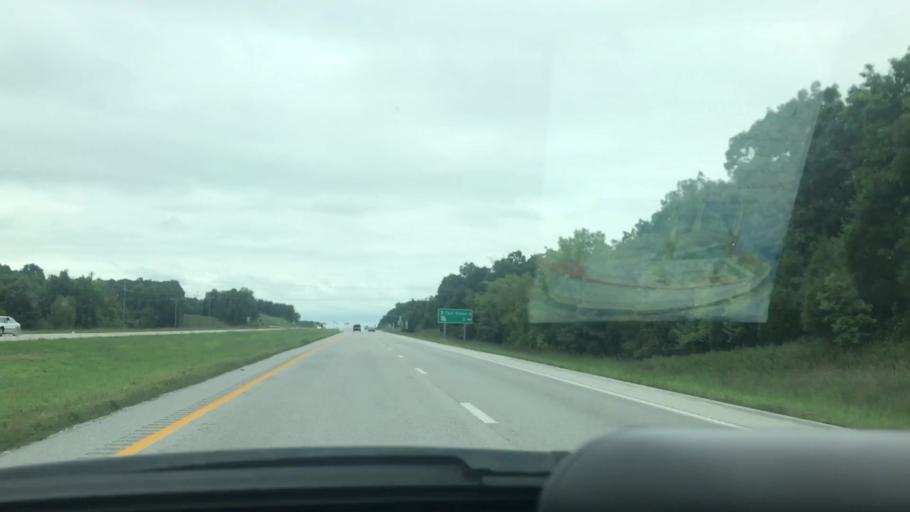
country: US
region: Missouri
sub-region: Greene County
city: Fair Grove
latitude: 37.3241
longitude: -93.1680
